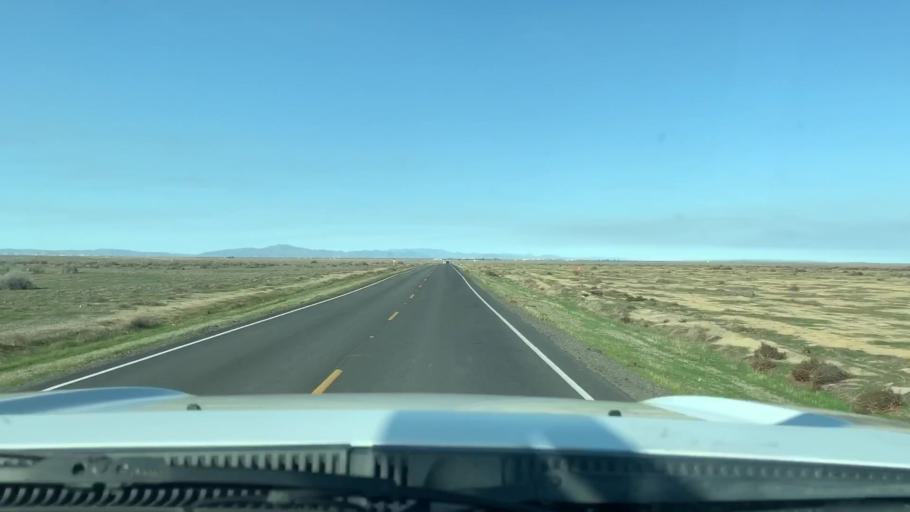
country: US
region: California
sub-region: Kern County
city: Lost Hills
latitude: 35.5653
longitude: -119.8067
